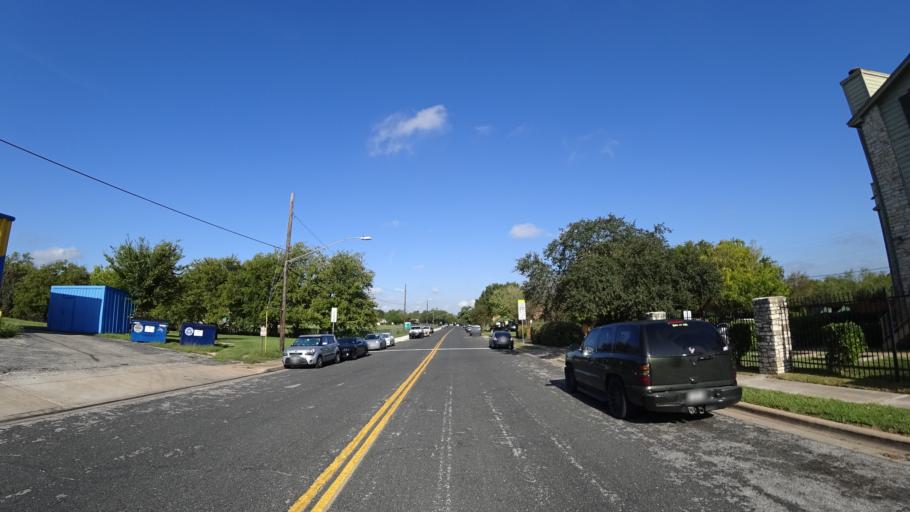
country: US
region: Texas
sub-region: Travis County
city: Rollingwood
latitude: 30.2107
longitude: -97.8040
